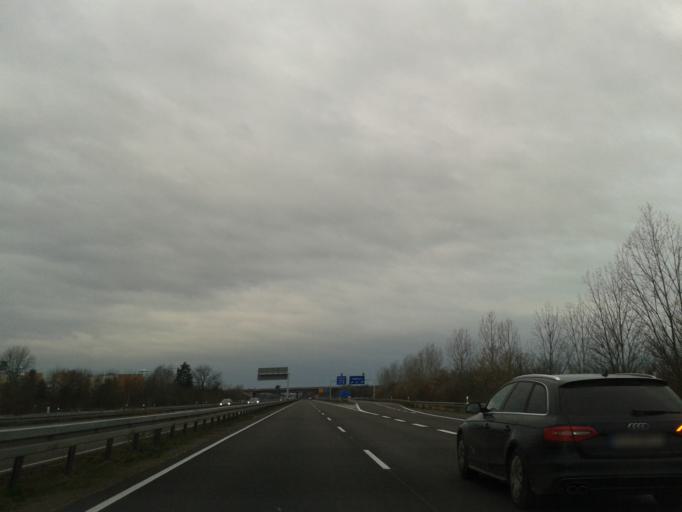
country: DE
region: Saxony-Anhalt
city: Peissen
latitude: 51.5086
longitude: 12.0518
